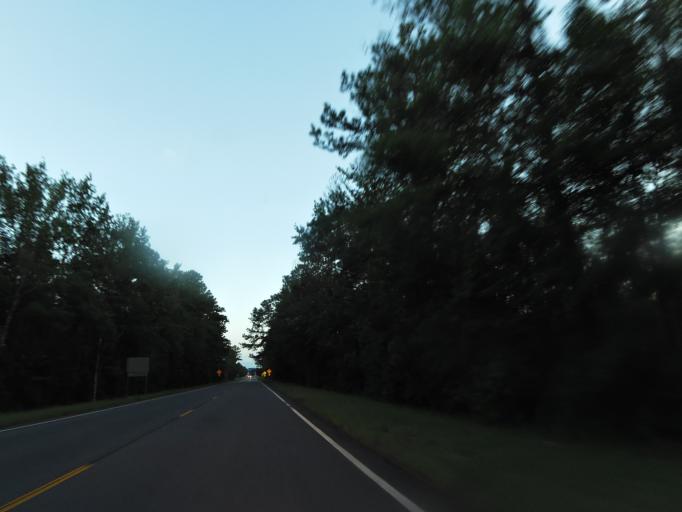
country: US
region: Georgia
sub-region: Camden County
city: Kingsland
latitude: 30.7463
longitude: -81.6878
